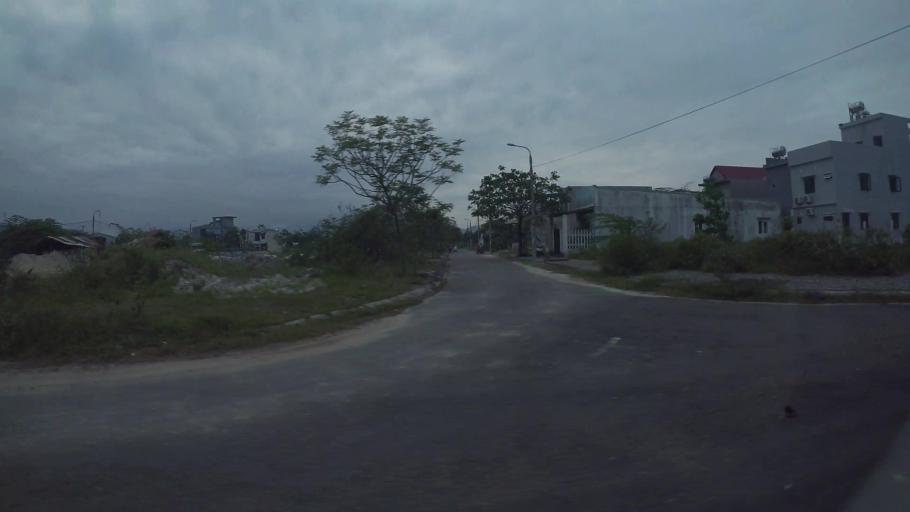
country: VN
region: Da Nang
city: Lien Chieu
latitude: 16.0716
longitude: 108.1085
